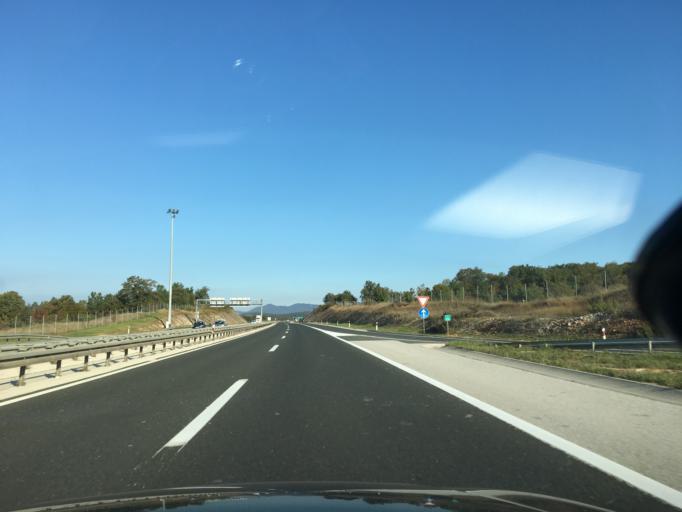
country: HR
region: Licko-Senjska
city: Gospic
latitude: 44.6706
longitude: 15.4190
